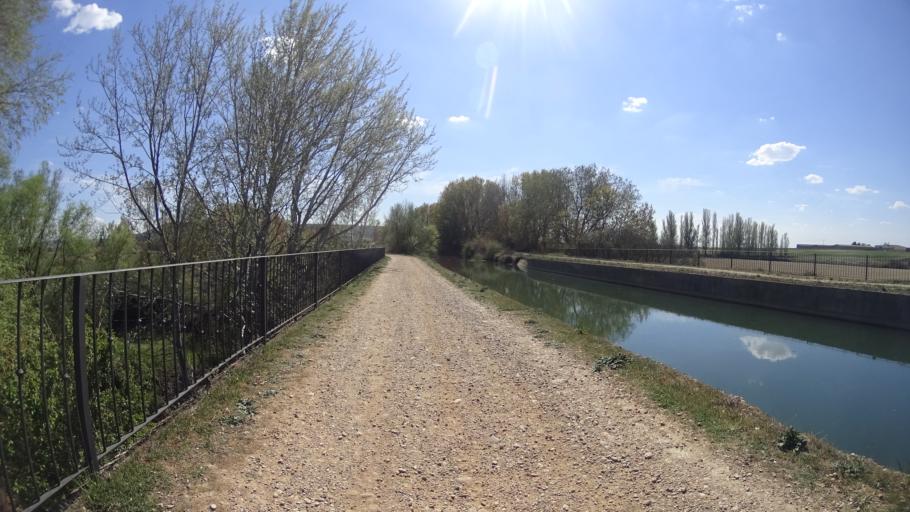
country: ES
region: Castille and Leon
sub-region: Provincia de Palencia
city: Grijota
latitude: 42.0428
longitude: -4.5851
